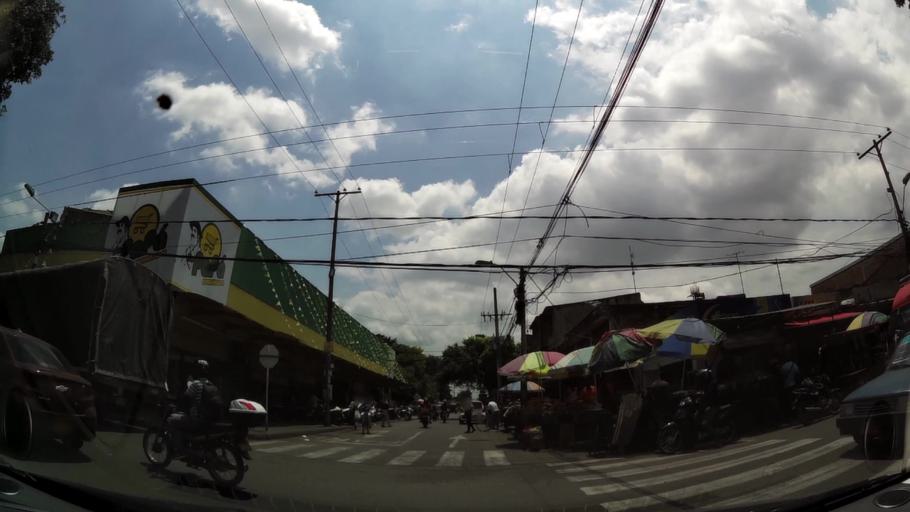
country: CO
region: Valle del Cauca
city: Cali
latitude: 3.4637
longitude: -76.4820
